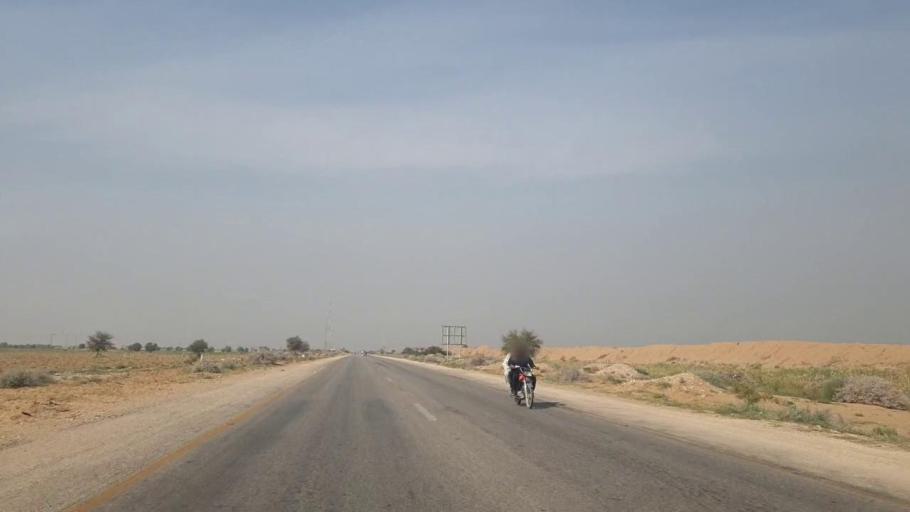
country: PK
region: Sindh
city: Sann
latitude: 26.0440
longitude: 68.1113
